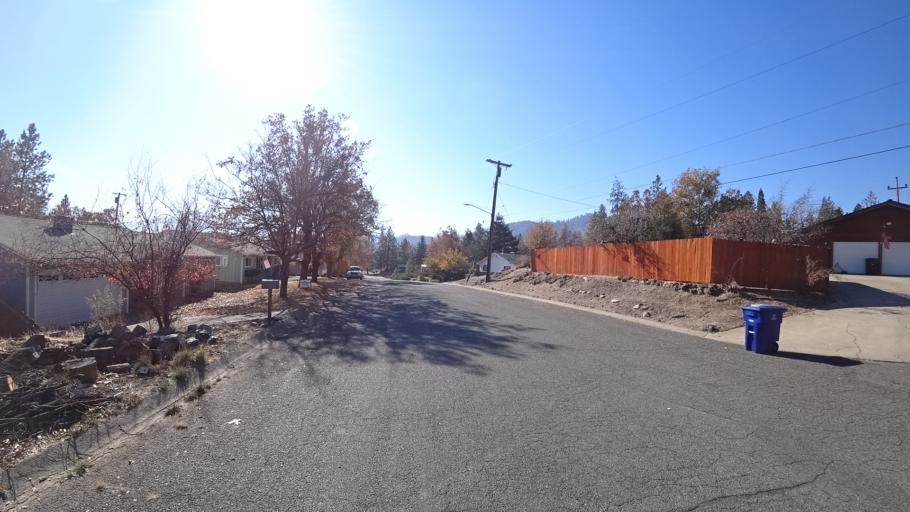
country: US
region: California
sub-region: Siskiyou County
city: Yreka
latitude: 41.7382
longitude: -122.6493
